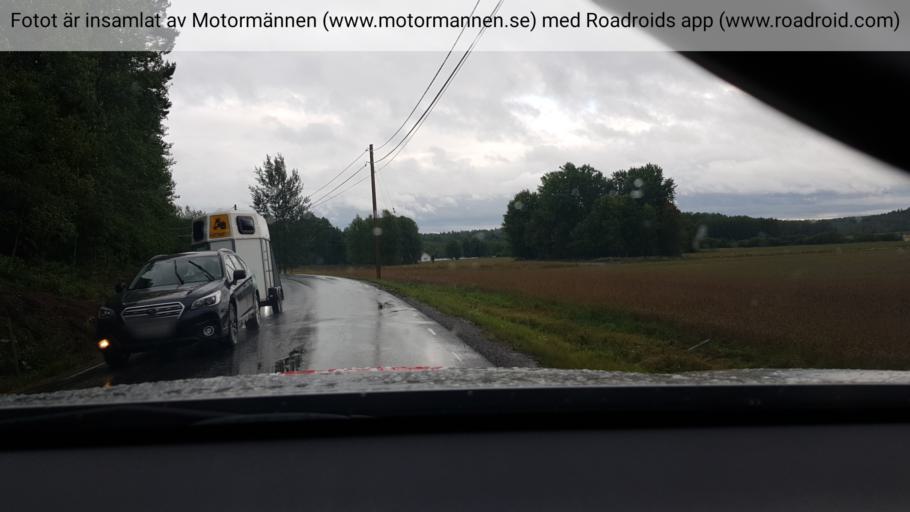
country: SE
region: Stockholm
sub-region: Haninge Kommun
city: Jordbro
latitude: 59.0930
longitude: 18.0370
